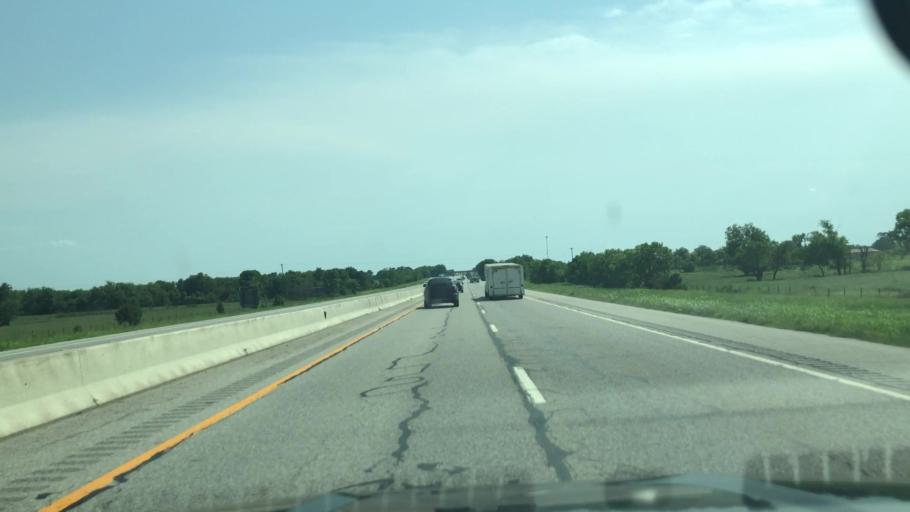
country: US
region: Oklahoma
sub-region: Ottawa County
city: Fairland
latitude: 36.7897
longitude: -94.8857
